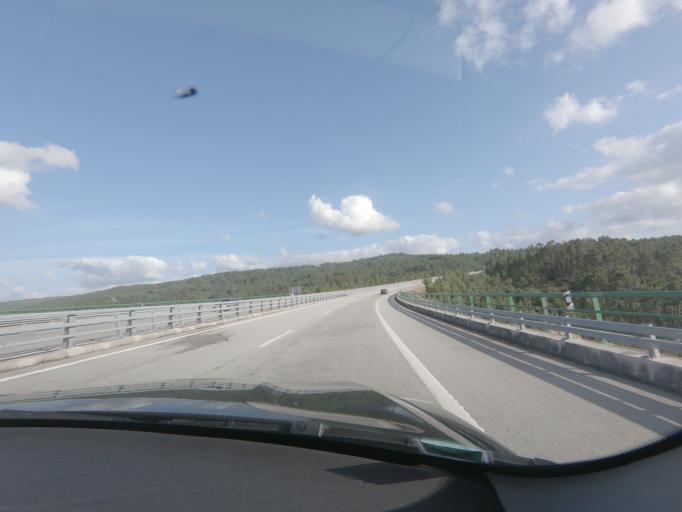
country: PT
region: Viseu
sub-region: Viseu
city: Campo
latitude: 40.7988
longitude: -7.9286
